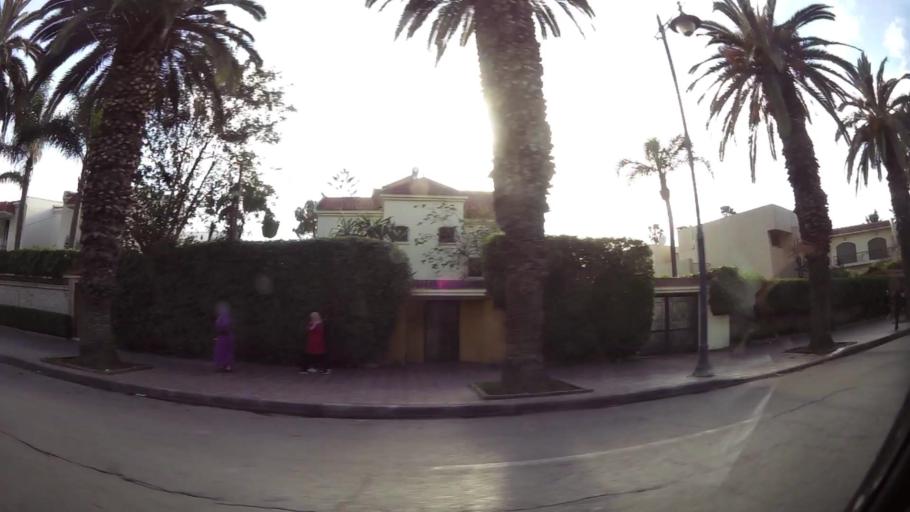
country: MA
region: Grand Casablanca
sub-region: Mohammedia
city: Mohammedia
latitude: 33.7026
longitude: -7.3943
